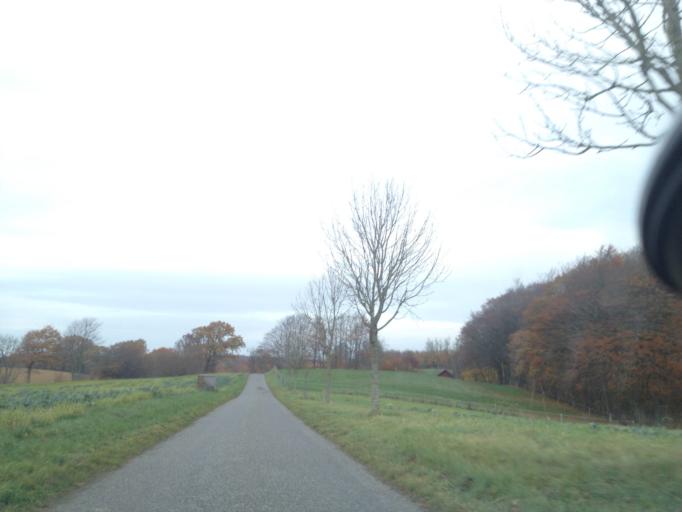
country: DK
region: South Denmark
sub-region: Assens Kommune
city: Vissenbjerg
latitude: 55.4319
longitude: 10.1659
